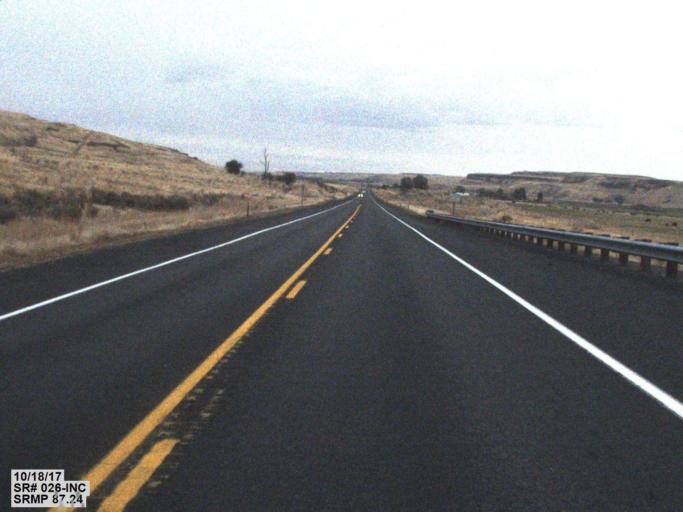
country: US
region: Washington
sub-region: Adams County
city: Ritzville
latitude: 46.7419
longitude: -118.2250
